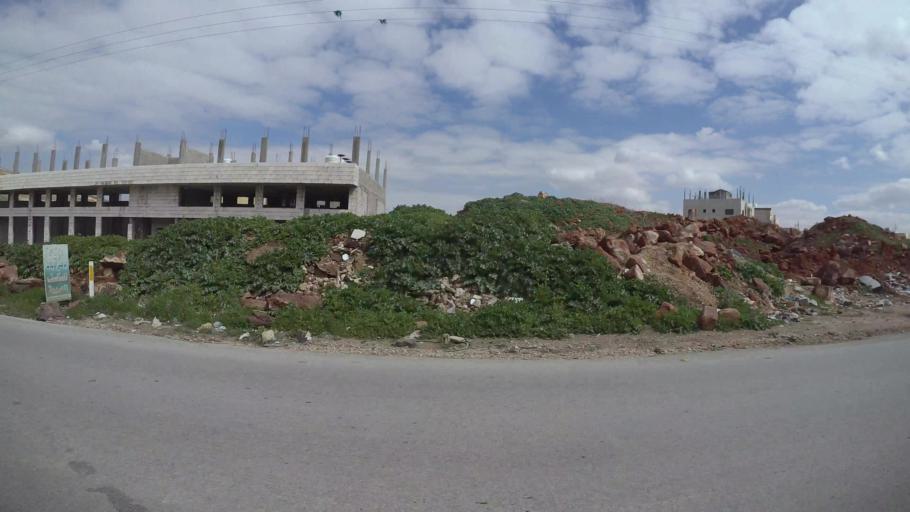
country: JO
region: Amman
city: Al Jubayhah
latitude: 32.0611
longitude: 35.8095
